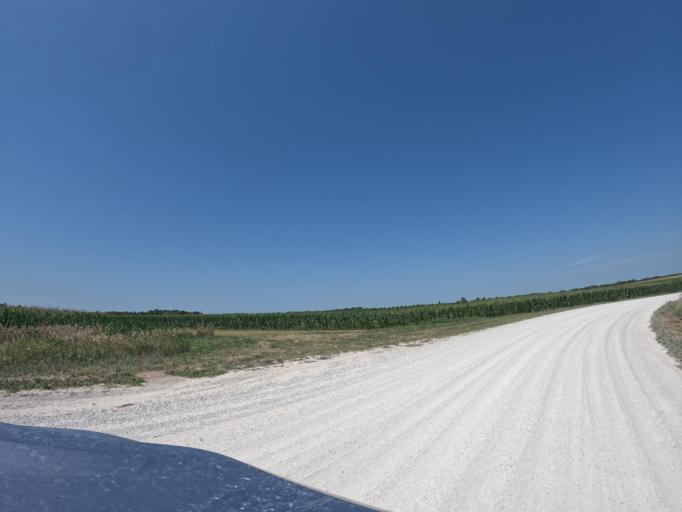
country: US
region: Iowa
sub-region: Henry County
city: Mount Pleasant
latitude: 40.8875
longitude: -91.5741
